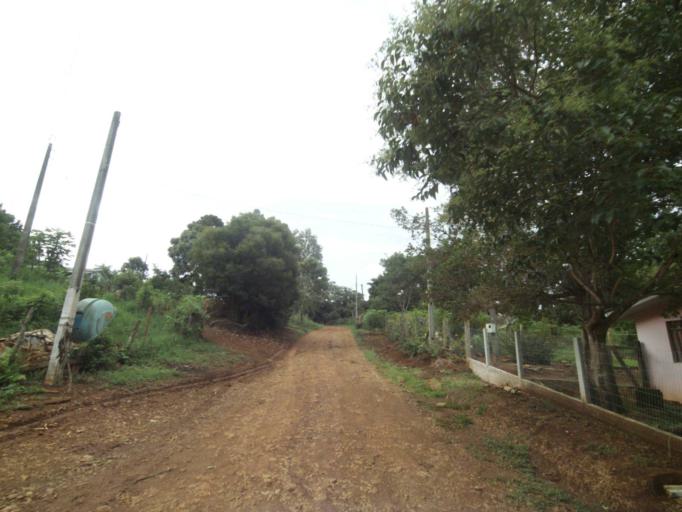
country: BR
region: Parana
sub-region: Pitanga
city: Pitanga
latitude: -24.8968
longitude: -51.9644
